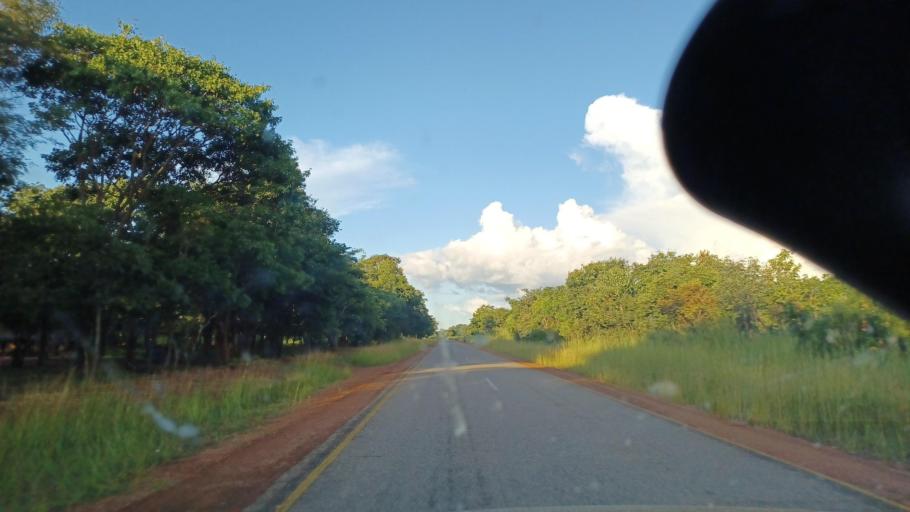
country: ZM
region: North-Western
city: Kalengwa
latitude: -13.1377
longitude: 25.1557
